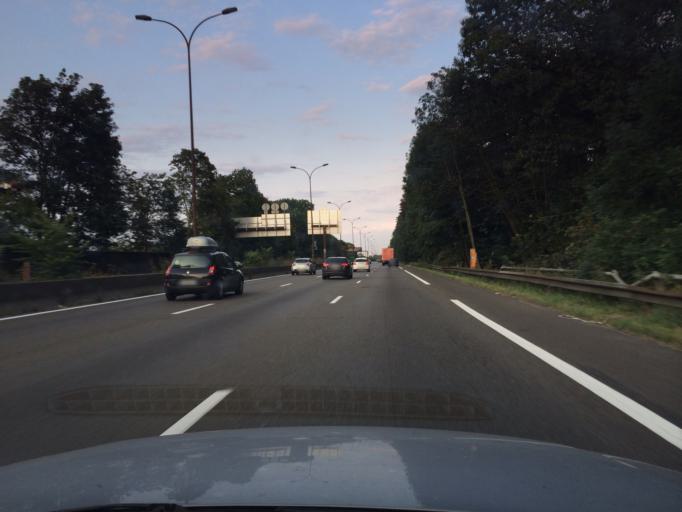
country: FR
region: Ile-de-France
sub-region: Departement des Hauts-de-Seine
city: Marnes-la-Coquette
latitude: 48.8338
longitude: 2.1650
